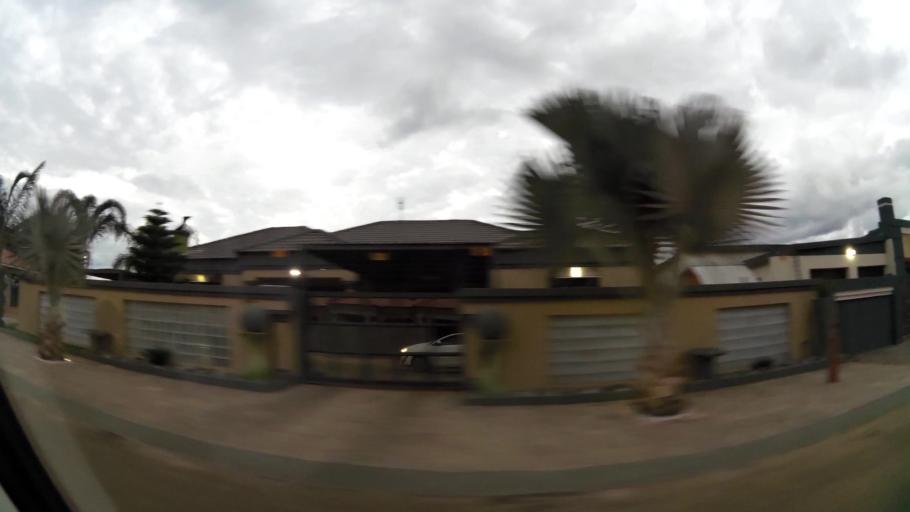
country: ZA
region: Limpopo
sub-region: Waterberg District Municipality
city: Mokopane
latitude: -24.1976
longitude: 28.9951
